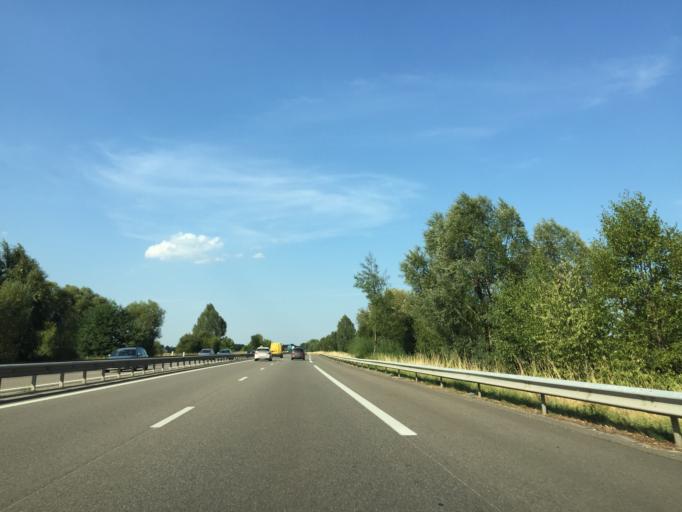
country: FR
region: Alsace
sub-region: Departement du Bas-Rhin
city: Valff
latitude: 48.4227
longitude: 7.4877
